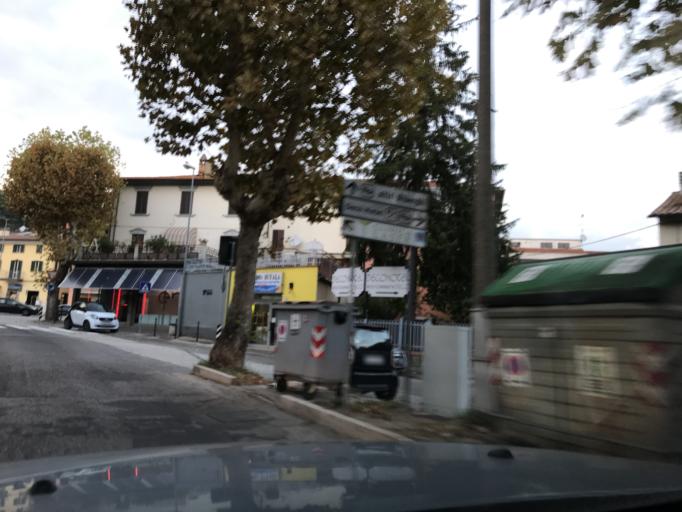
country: IT
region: Umbria
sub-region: Provincia di Perugia
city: Via Lippia
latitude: 43.0911
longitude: 12.4453
